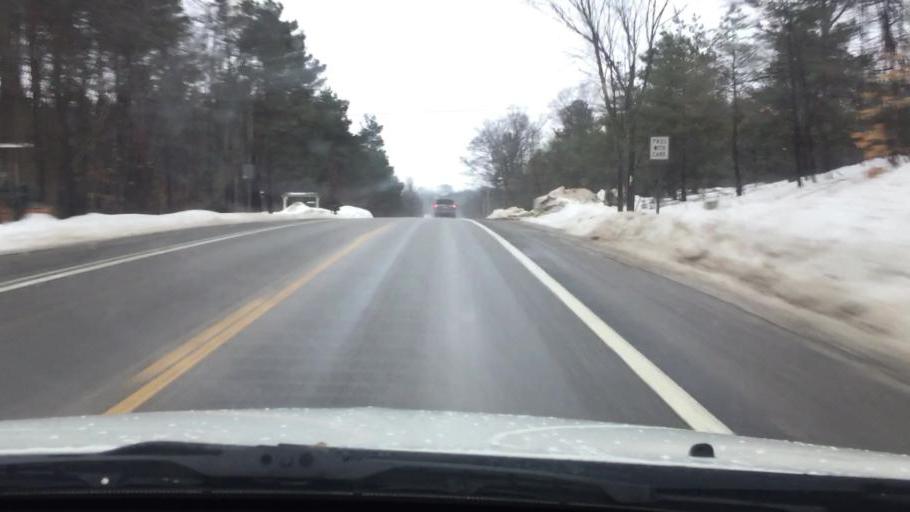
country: US
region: Michigan
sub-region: Charlevoix County
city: East Jordan
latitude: 45.2394
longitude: -85.1813
